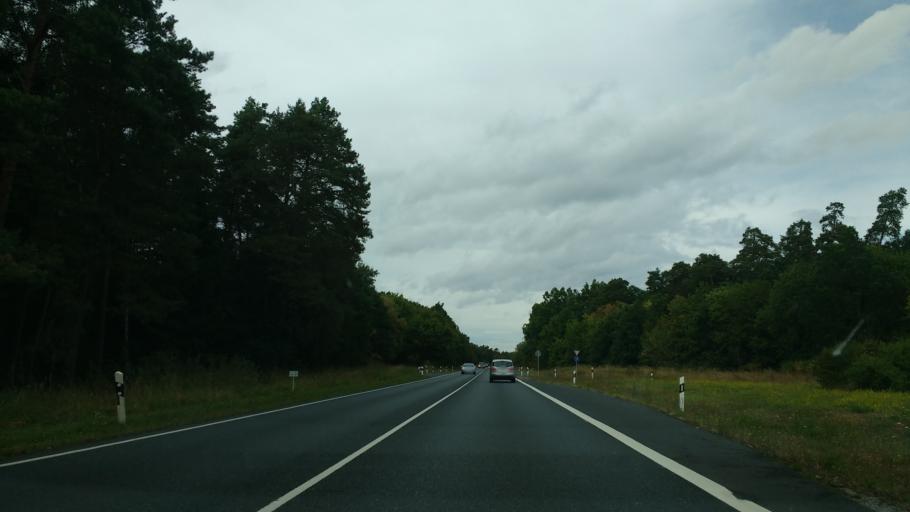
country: DE
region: Bavaria
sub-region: Regierungsbezirk Unterfranken
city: Schwebheim
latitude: 50.0105
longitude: 10.2386
